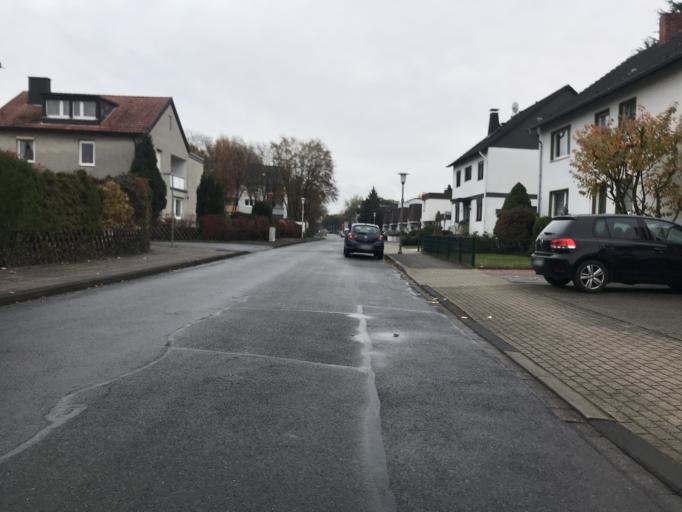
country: DE
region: North Rhine-Westphalia
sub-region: Regierungsbezirk Arnsberg
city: Hamm
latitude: 51.6931
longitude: 7.8680
